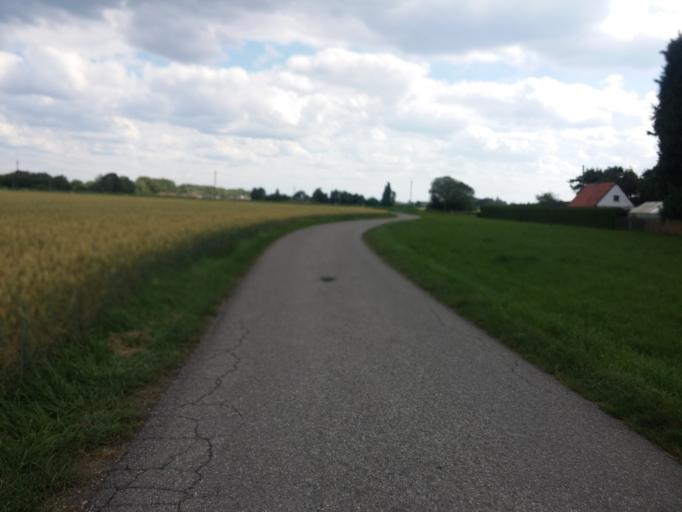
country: DE
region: Bavaria
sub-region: Upper Bavaria
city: Unterfoehring
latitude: 48.1605
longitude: 11.6653
